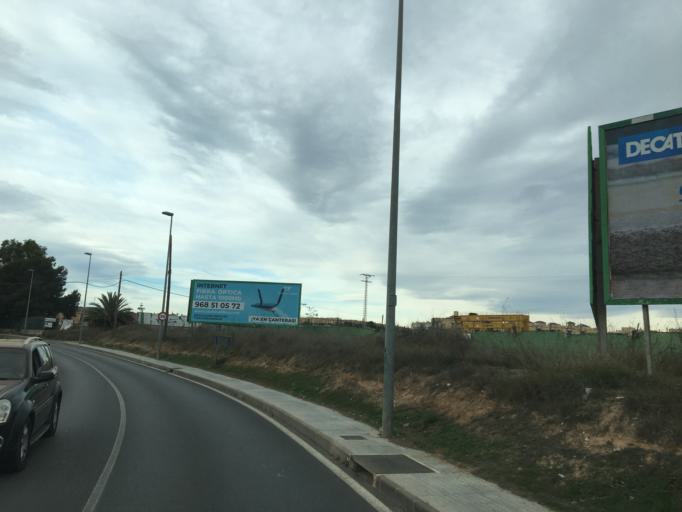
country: ES
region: Murcia
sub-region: Murcia
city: Cartagena
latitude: 37.6139
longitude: -1.0165
